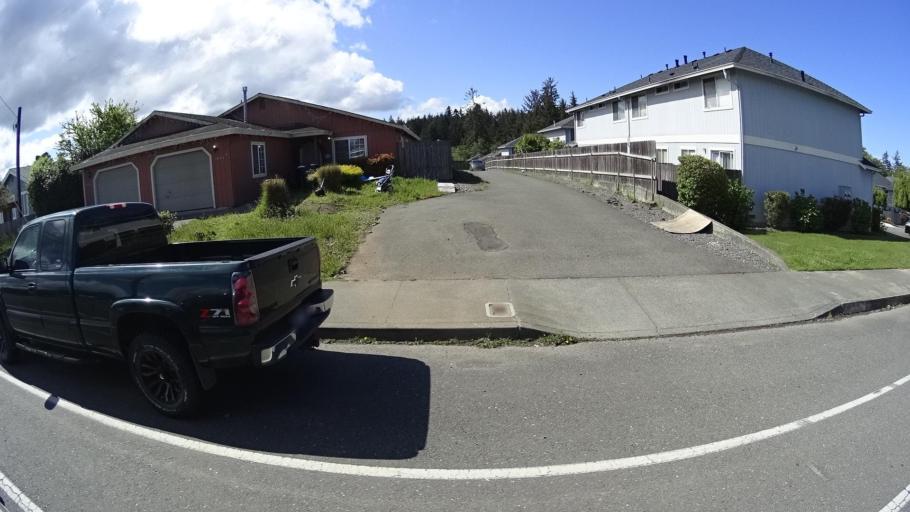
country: US
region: California
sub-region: Humboldt County
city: McKinleyville
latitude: 40.9358
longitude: -124.0934
